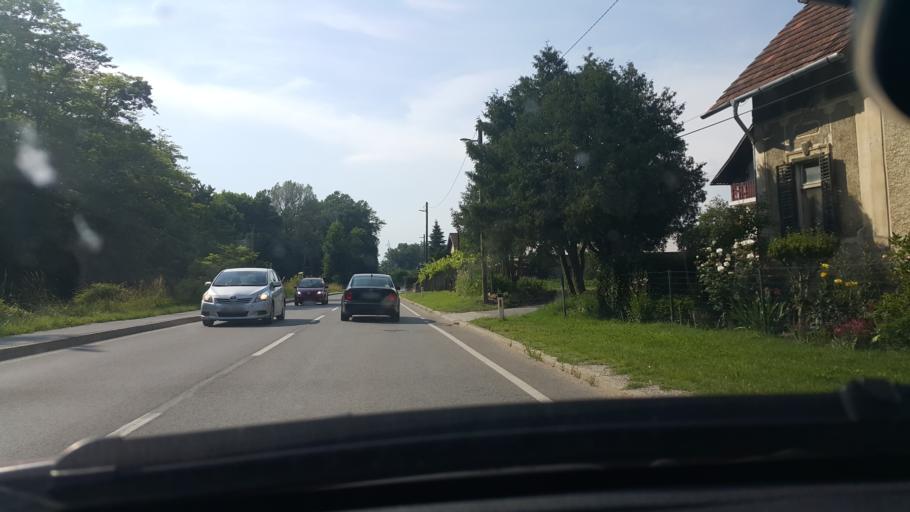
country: SI
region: Duplek
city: Zgornji Duplek
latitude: 46.5096
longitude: 15.7220
